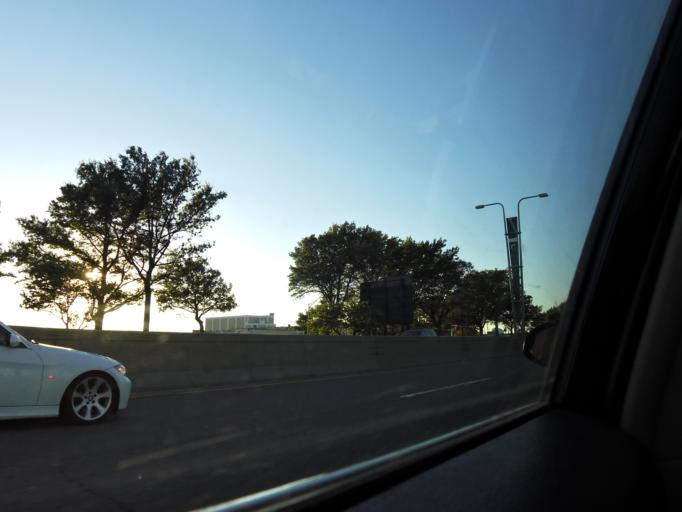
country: US
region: New York
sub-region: Queens County
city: Jamaica
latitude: 40.6501
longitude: -73.8046
